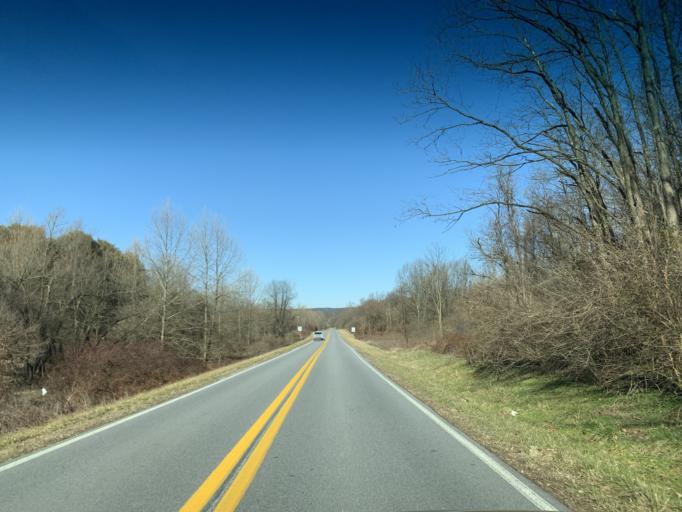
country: US
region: Maryland
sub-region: Carroll County
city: Westminster
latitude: 39.6446
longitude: -76.9634
